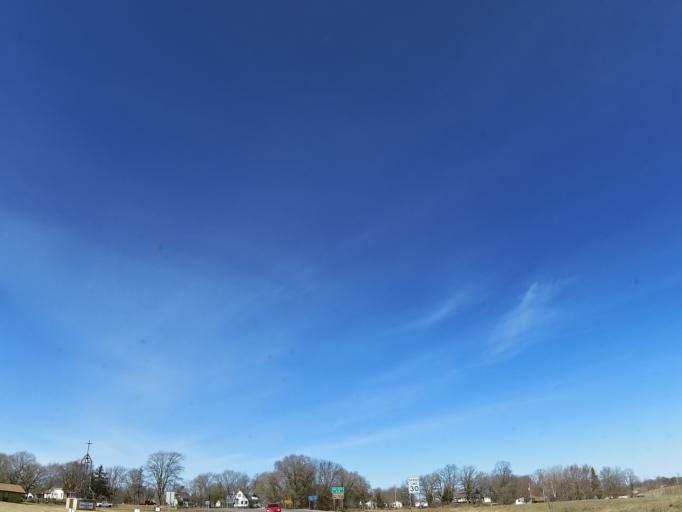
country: US
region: Minnesota
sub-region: Wright County
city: Annandale
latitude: 45.2914
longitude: -94.2102
